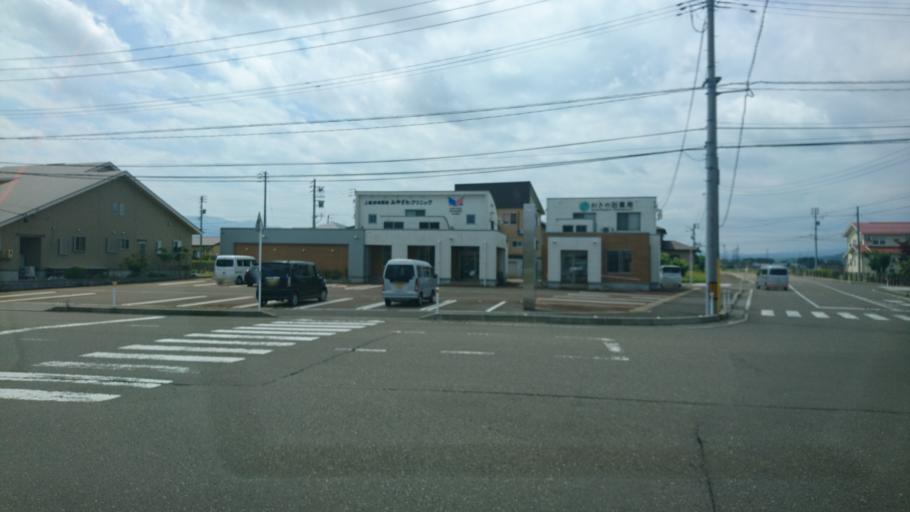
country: JP
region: Niigata
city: Joetsu
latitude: 37.0787
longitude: 138.2470
